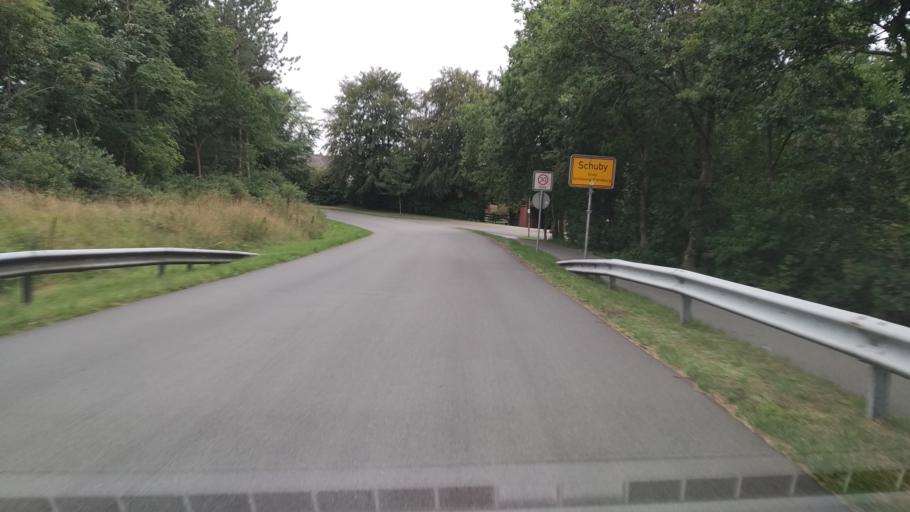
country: DE
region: Schleswig-Holstein
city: Schuby
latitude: 54.5255
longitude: 9.4843
